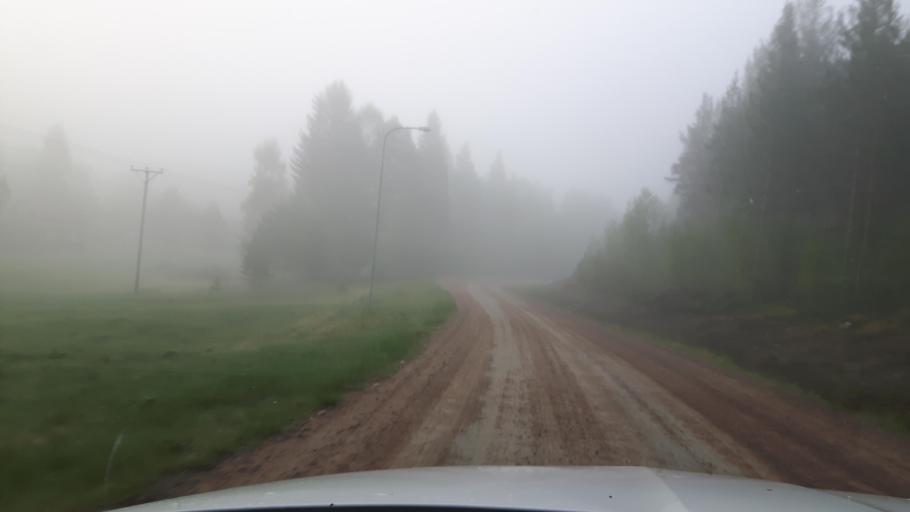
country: SE
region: Vaesternorrland
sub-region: Ange Kommun
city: Ange
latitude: 62.1747
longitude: 15.6373
